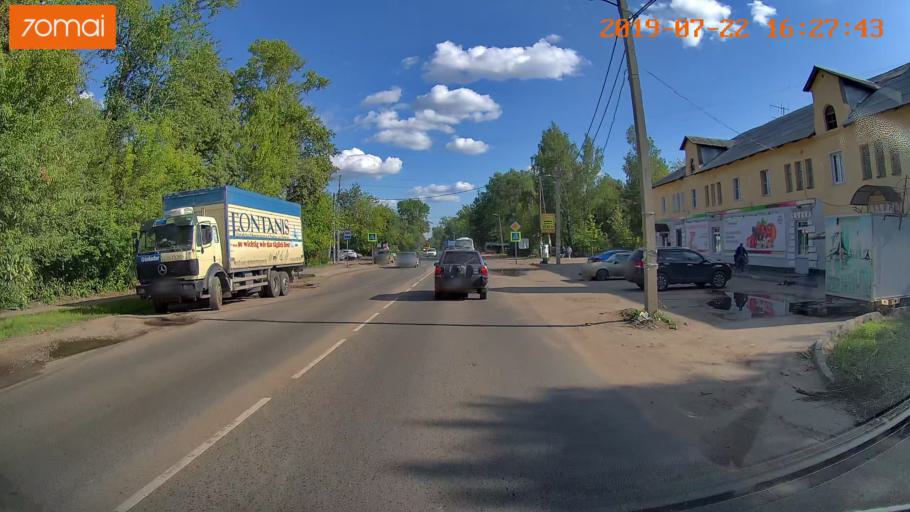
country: RU
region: Ivanovo
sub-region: Gorod Ivanovo
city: Ivanovo
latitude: 57.0423
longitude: 40.9472
